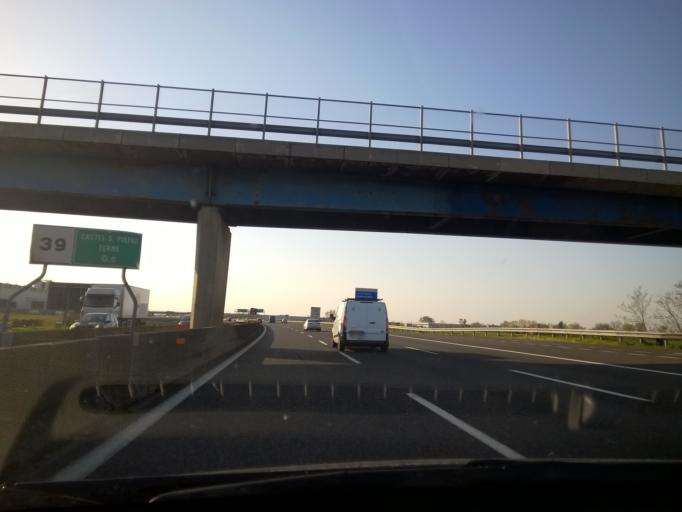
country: IT
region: Emilia-Romagna
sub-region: Provincia di Bologna
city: Castel San Pietro Terme
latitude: 44.4230
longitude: 11.6165
